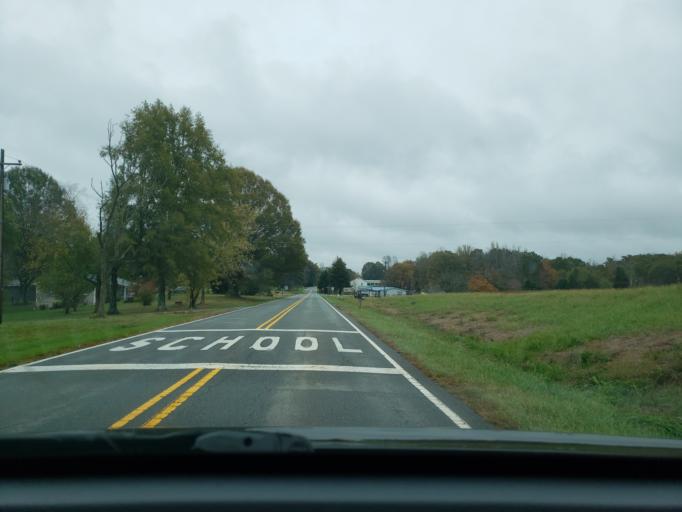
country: US
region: North Carolina
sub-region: Stokes County
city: Walnut Cove
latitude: 36.3279
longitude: -80.1458
